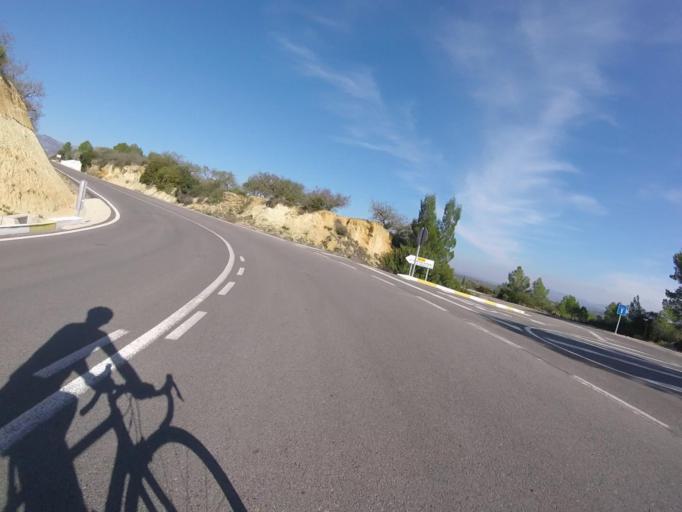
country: ES
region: Valencia
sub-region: Provincia de Castello
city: Cuevas de Vinroma
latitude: 40.2593
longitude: 0.0805
